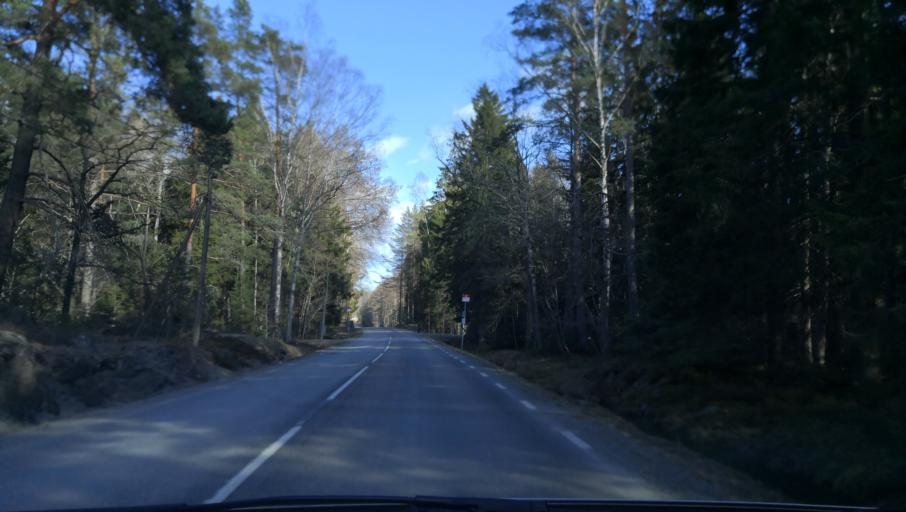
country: SE
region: Stockholm
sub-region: Varmdo Kommun
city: Hemmesta
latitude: 59.3567
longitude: 18.5702
